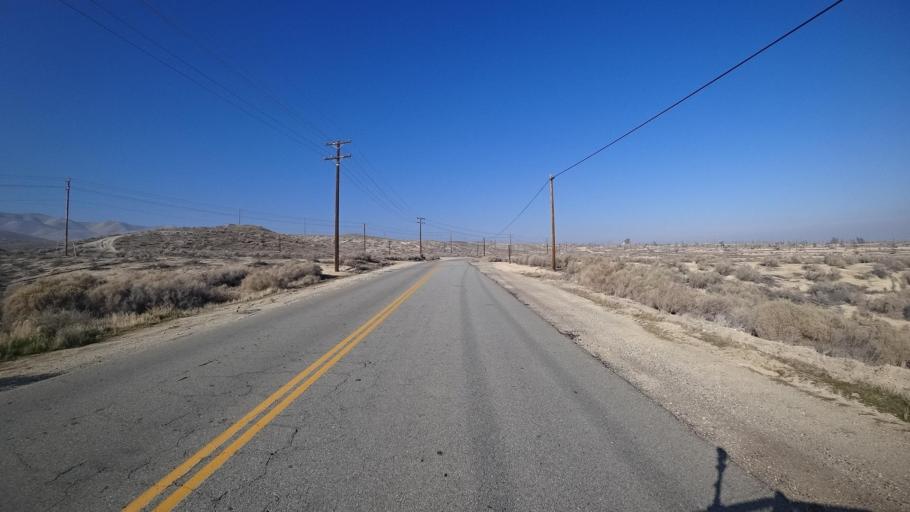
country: US
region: California
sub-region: Kern County
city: Taft Heights
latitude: 35.1964
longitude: -119.5866
